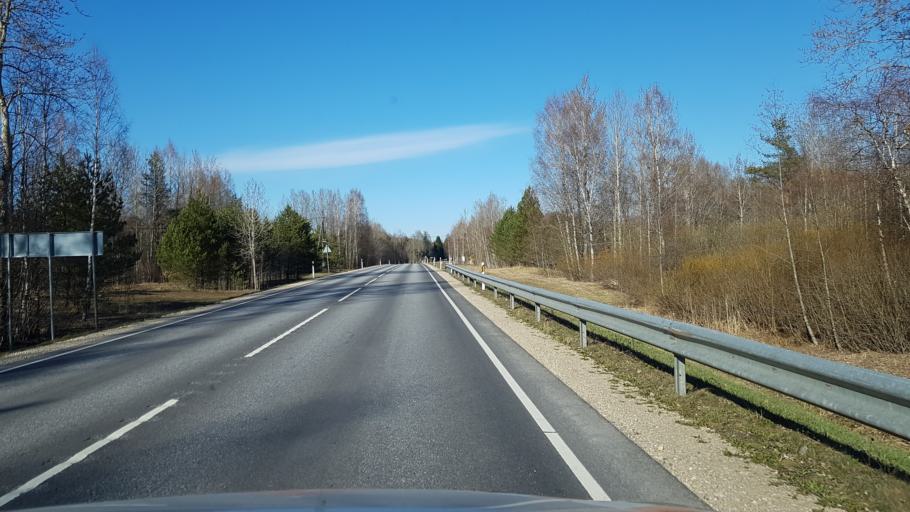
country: EE
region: Jogevamaa
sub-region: Mustvee linn
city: Mustvee
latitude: 58.9493
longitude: 27.0580
